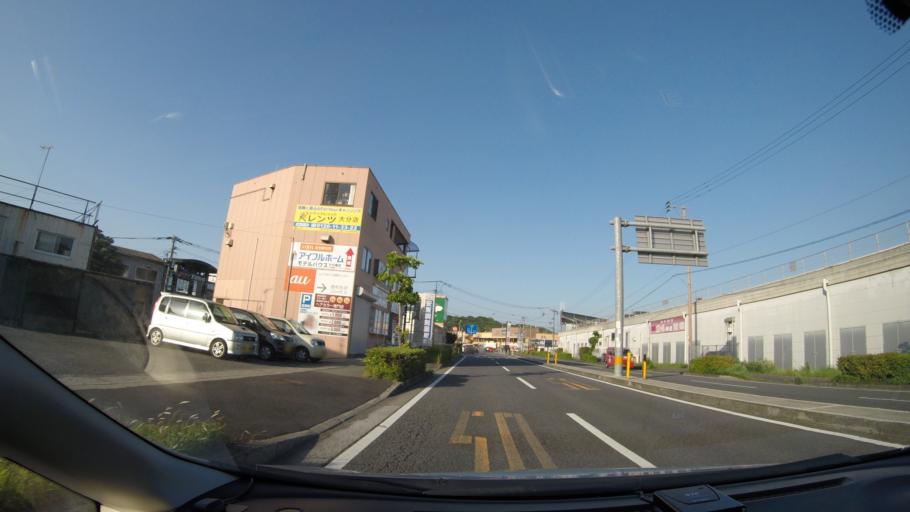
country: JP
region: Oita
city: Oita
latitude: 33.1996
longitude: 131.6054
